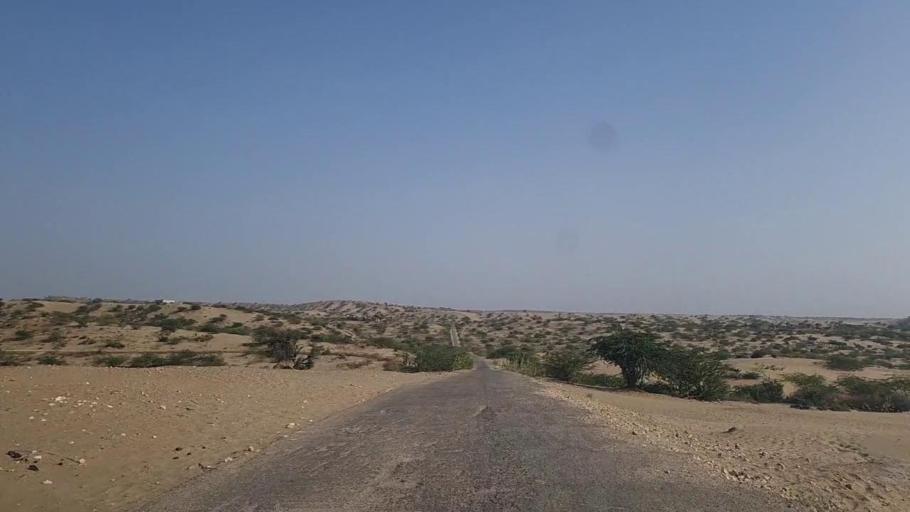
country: PK
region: Sindh
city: Naukot
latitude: 24.6278
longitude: 69.3646
